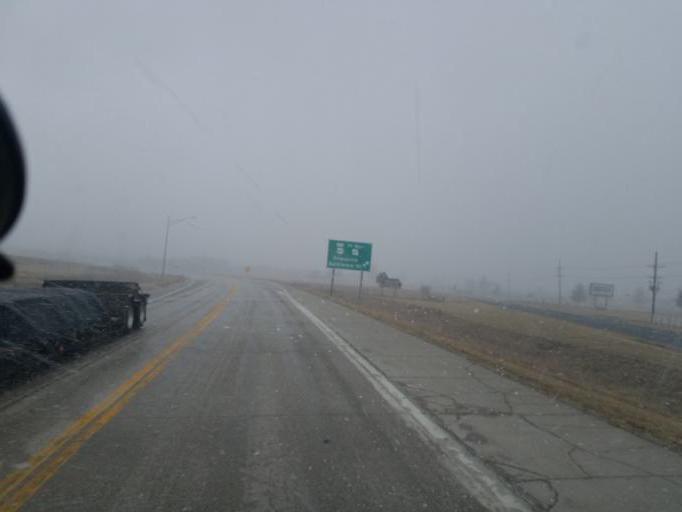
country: US
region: Missouri
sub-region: Adair County
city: Kirksville
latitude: 40.2436
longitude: -92.5823
